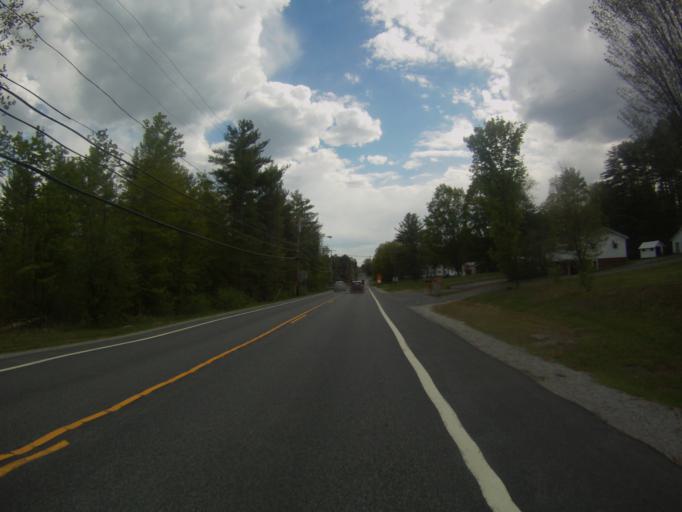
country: US
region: New York
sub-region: Essex County
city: Ticonderoga
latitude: 43.8491
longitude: -73.7579
